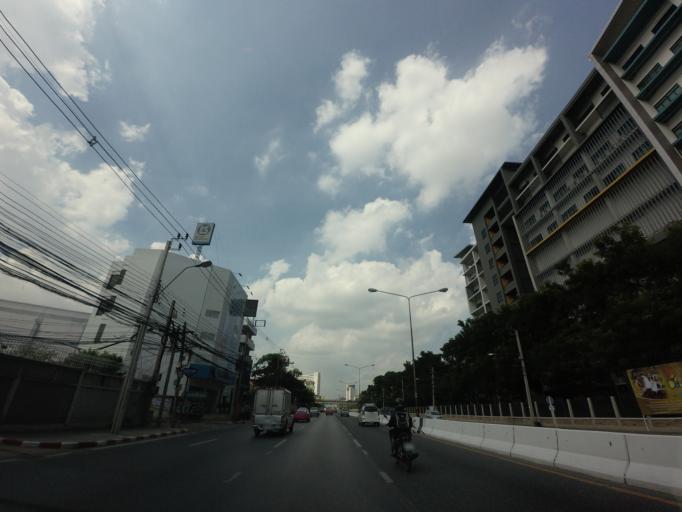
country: TH
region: Bangkok
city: Chatuchak
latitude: 13.8440
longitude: 100.5678
